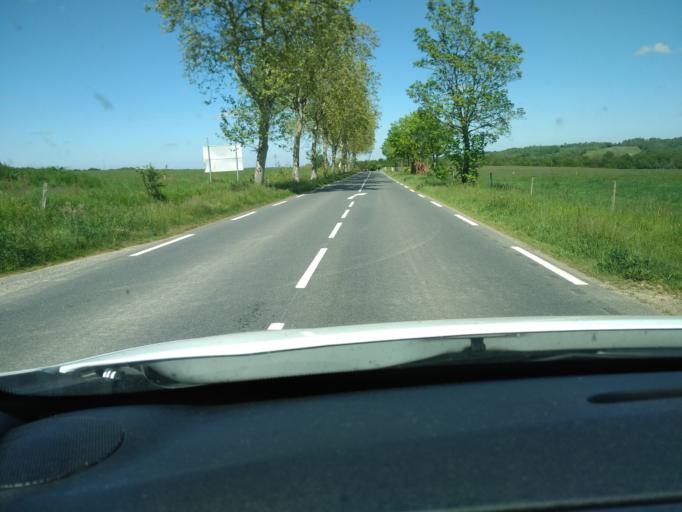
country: FR
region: Midi-Pyrenees
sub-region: Departement de la Haute-Garonne
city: Boulogne-sur-Gesse
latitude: 43.3015
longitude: 0.6727
